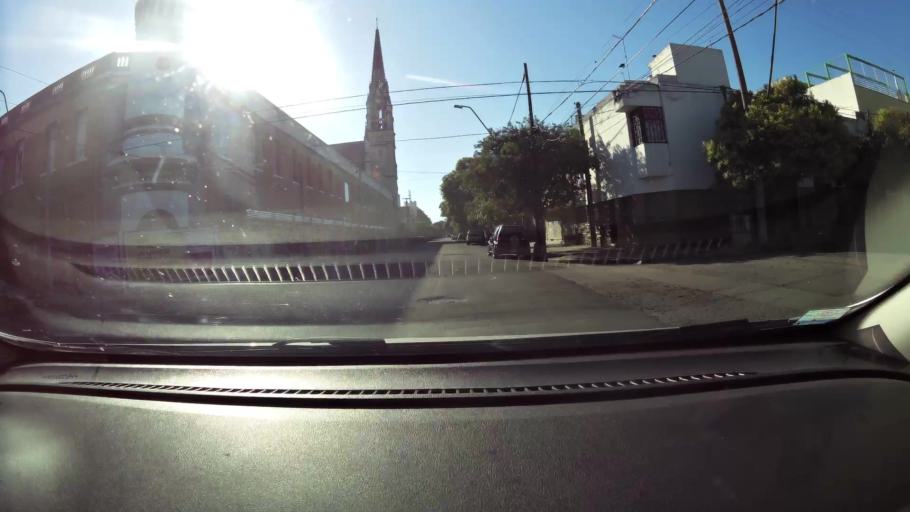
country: AR
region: Cordoba
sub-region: Departamento de Capital
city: Cordoba
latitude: -31.3947
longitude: -64.1810
